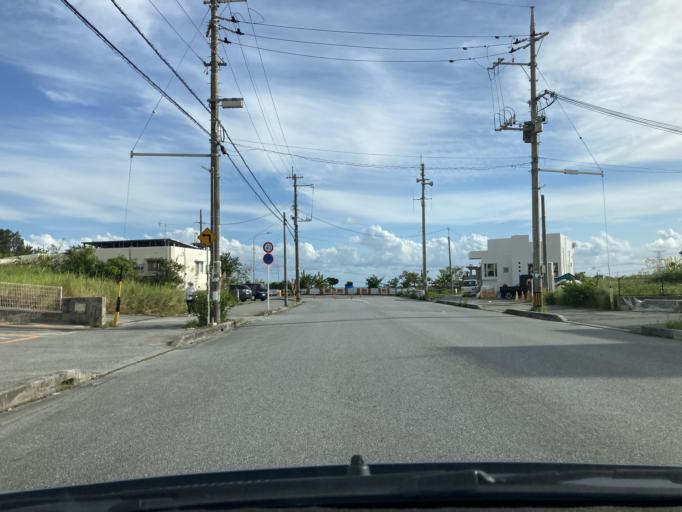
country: JP
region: Okinawa
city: Okinawa
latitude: 26.3387
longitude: 127.8259
